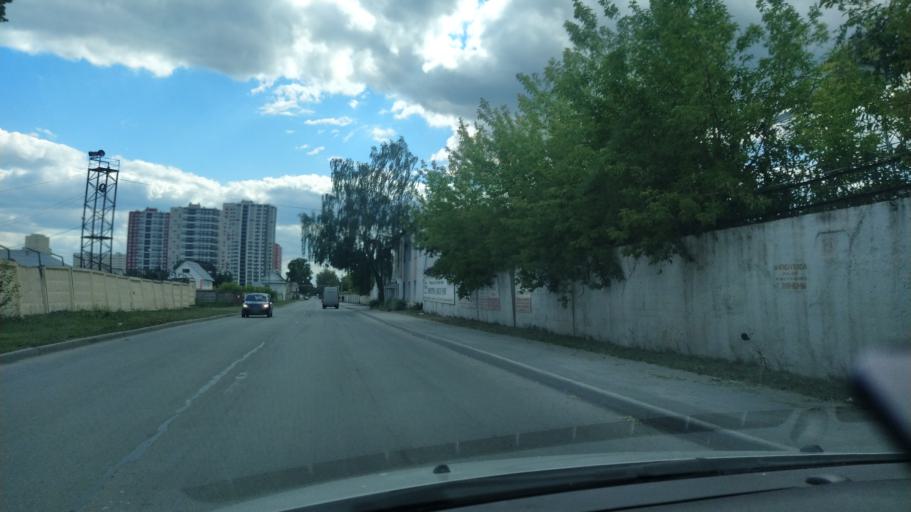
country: RU
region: Sverdlovsk
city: Shuvakish
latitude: 56.8821
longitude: 60.5291
